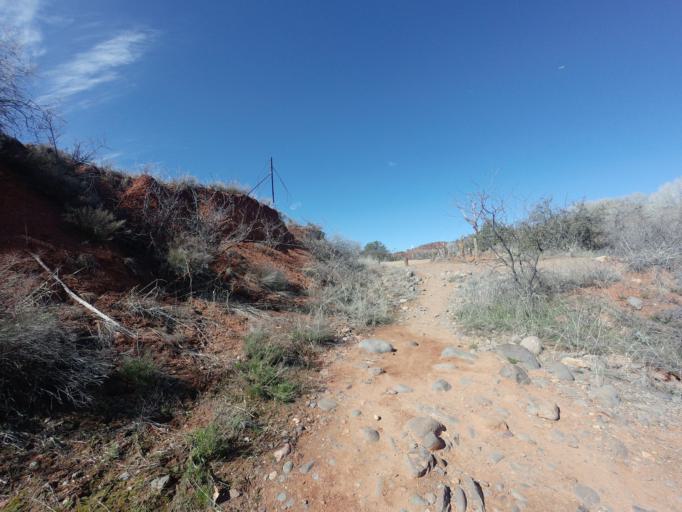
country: US
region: Arizona
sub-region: Yavapai County
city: West Sedona
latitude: 34.8248
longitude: -111.8077
